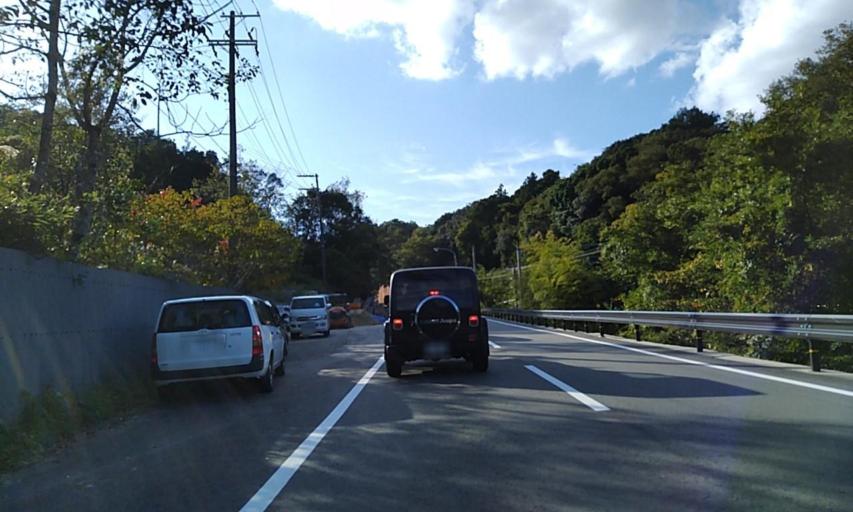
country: JP
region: Wakayama
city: Tanabe
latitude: 33.6828
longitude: 135.4006
